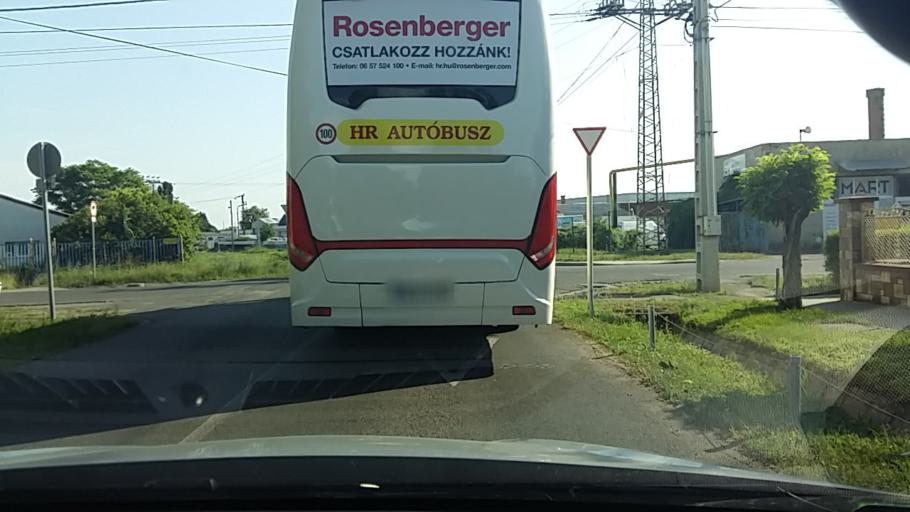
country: HU
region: Heves
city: Gyongyos
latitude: 47.7672
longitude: 19.9205
